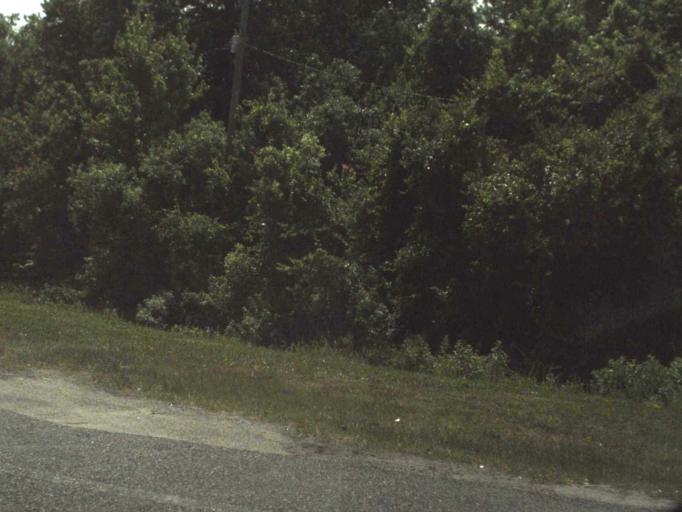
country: US
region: Florida
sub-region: Seminole County
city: Heathrow
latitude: 28.8112
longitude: -81.3477
